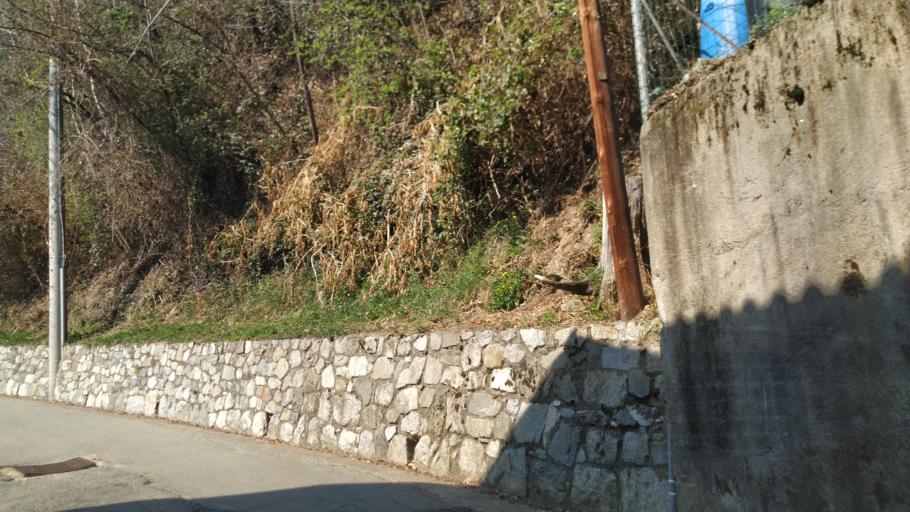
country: IT
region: Piedmont
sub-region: Provincia di Biella
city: Frazione Chiesa
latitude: 45.6869
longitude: 8.2003
